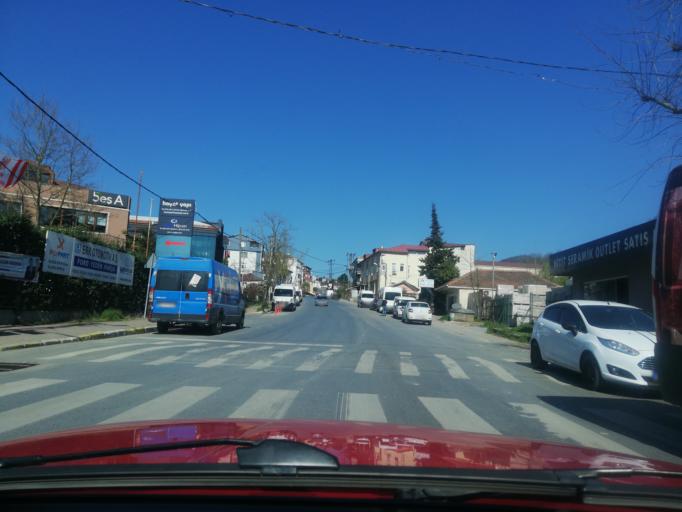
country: TR
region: Istanbul
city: Mahmut Sevket Pasa
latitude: 41.0967
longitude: 29.1488
